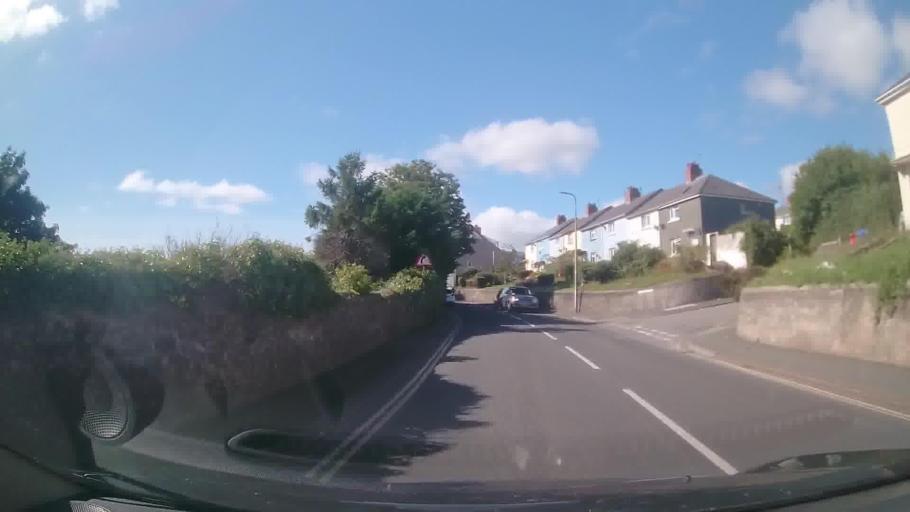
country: GB
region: Wales
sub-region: Pembrokeshire
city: Tenby
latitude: 51.6729
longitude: -4.7100
